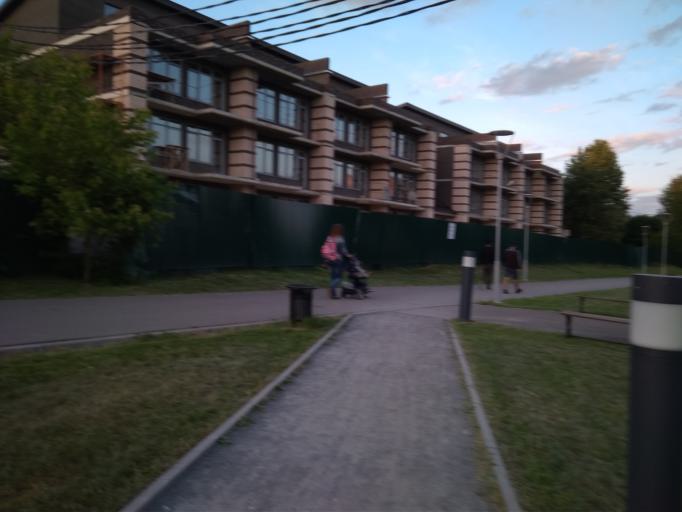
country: RU
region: Moskovskaya
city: Troitsk
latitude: 55.4958
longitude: 37.3027
